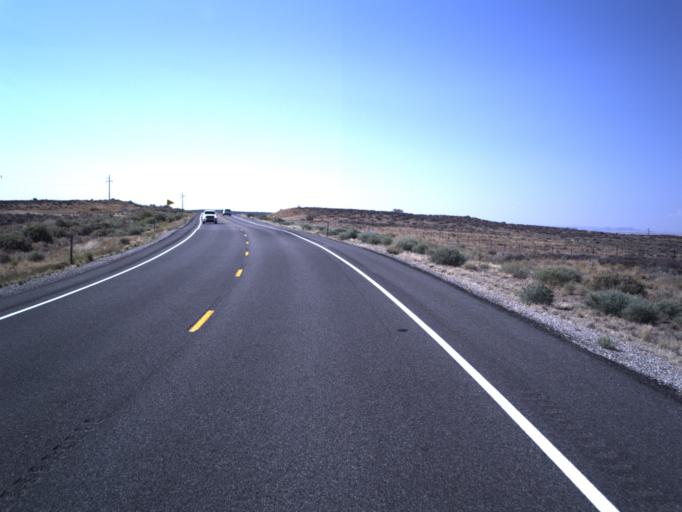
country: US
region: Utah
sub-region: San Juan County
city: Blanding
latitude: 37.3889
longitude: -109.5003
